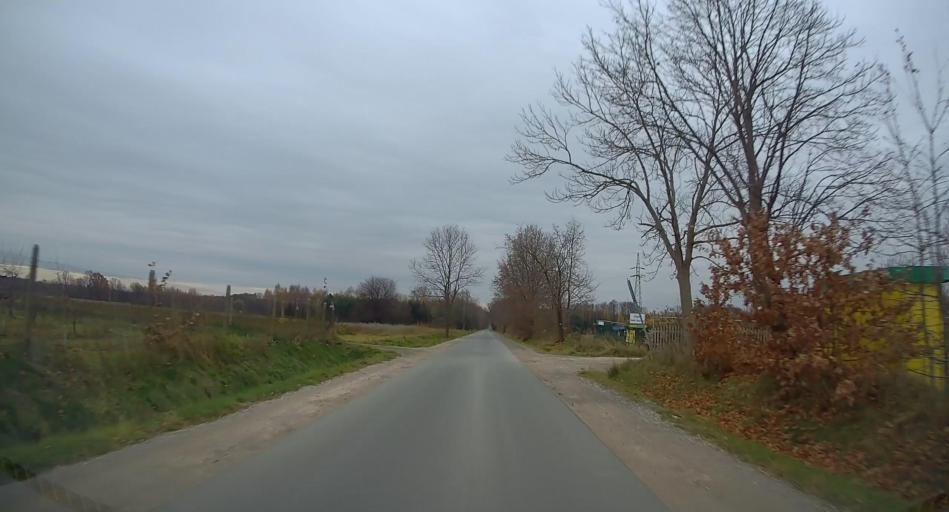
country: PL
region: Lodz Voivodeship
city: Zabia Wola
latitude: 52.0044
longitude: 20.6570
